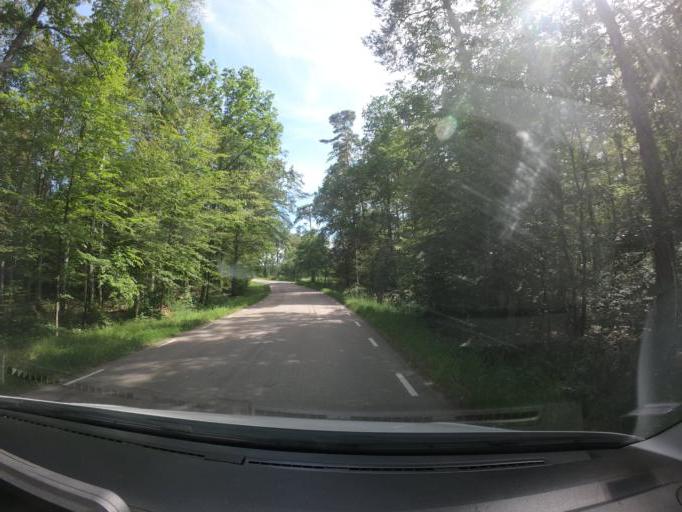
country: SE
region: Kronoberg
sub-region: Markaryds Kommun
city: Markaryd
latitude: 56.3985
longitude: 13.4502
